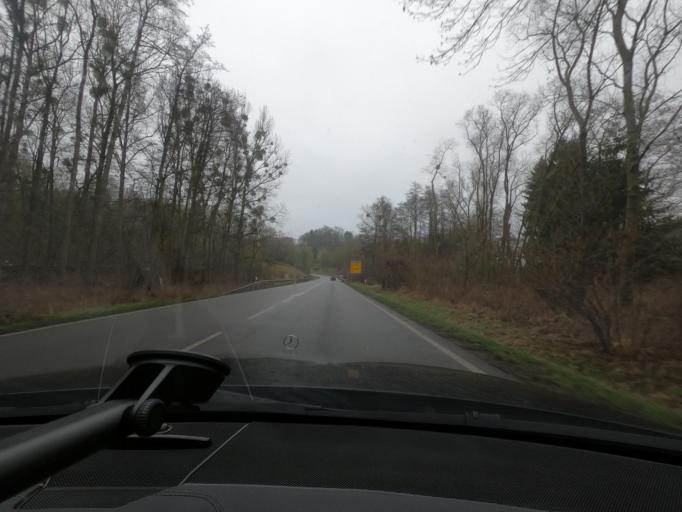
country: DE
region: Hesse
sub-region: Regierungsbezirk Kassel
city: Volkmarsen
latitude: 51.3488
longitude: 9.0823
